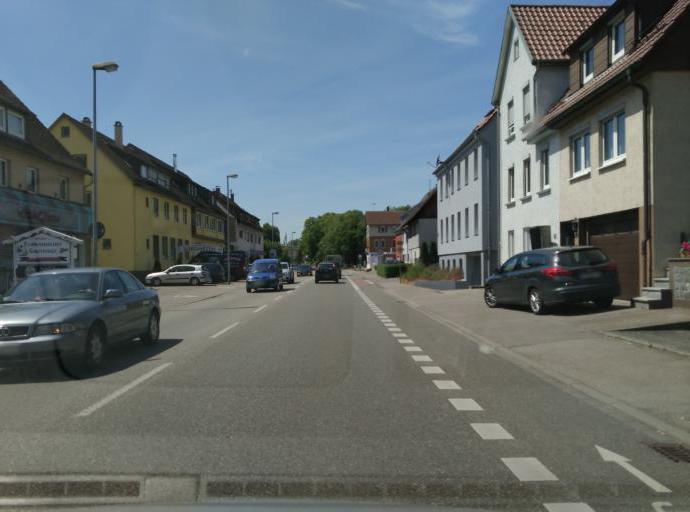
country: DE
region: Baden-Wuerttemberg
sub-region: Regierungsbezirk Stuttgart
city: Nurtingen
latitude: 48.6206
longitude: 9.3171
